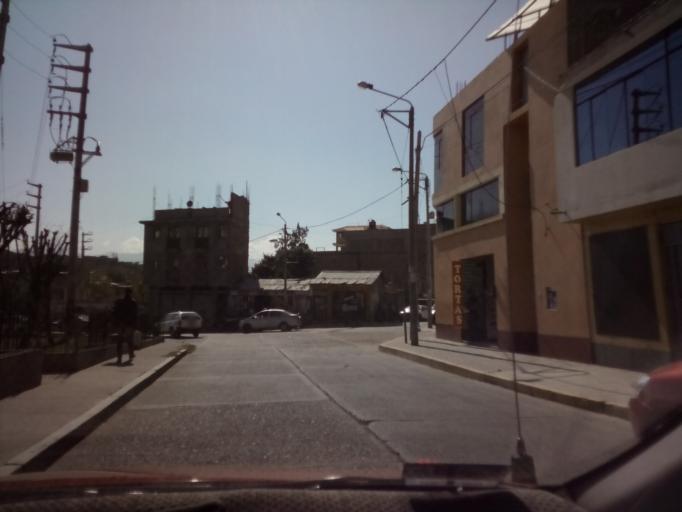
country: PE
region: Ayacucho
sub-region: Provincia de Huamanga
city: Ayacucho
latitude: -13.1635
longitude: -74.2228
